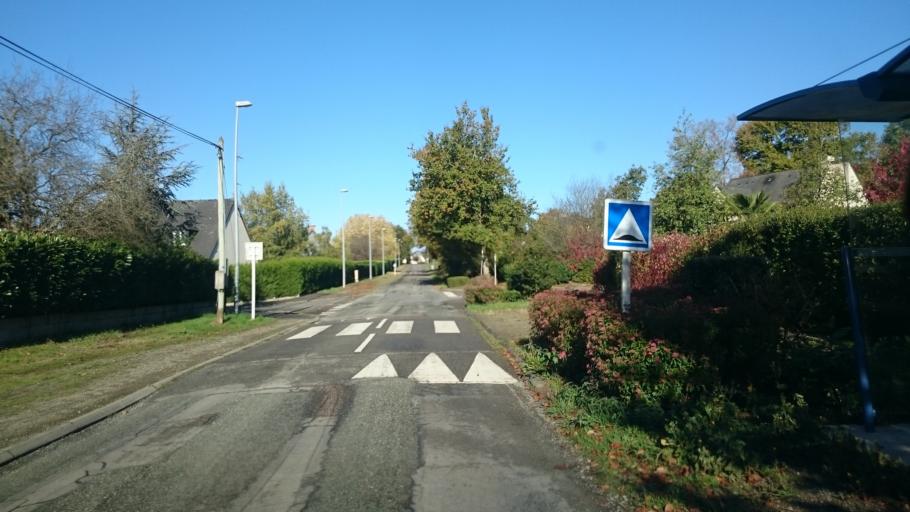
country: FR
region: Brittany
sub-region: Departement d'Ille-et-Vilaine
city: Laille
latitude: 47.9736
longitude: -1.7148
